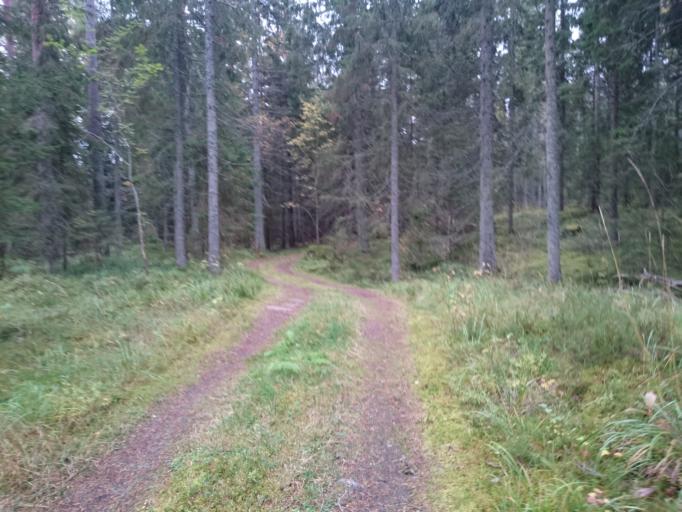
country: SE
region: OErebro
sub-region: Laxa Kommun
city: Laxa
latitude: 58.7644
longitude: 14.5953
